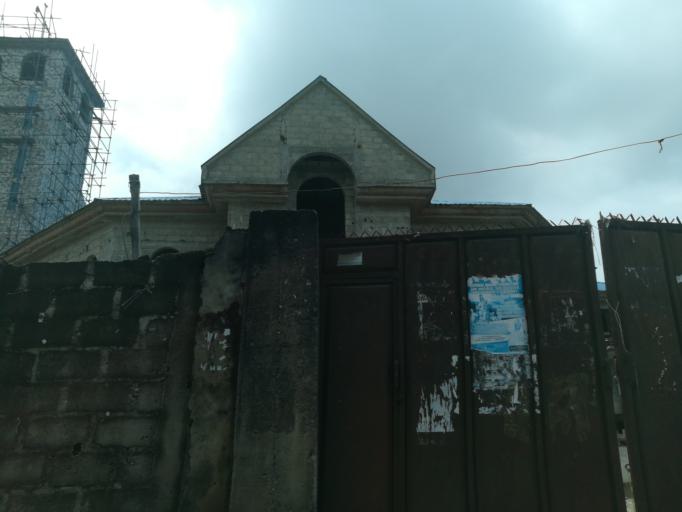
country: NG
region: Rivers
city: Port Harcourt
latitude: 4.8894
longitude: 7.0013
